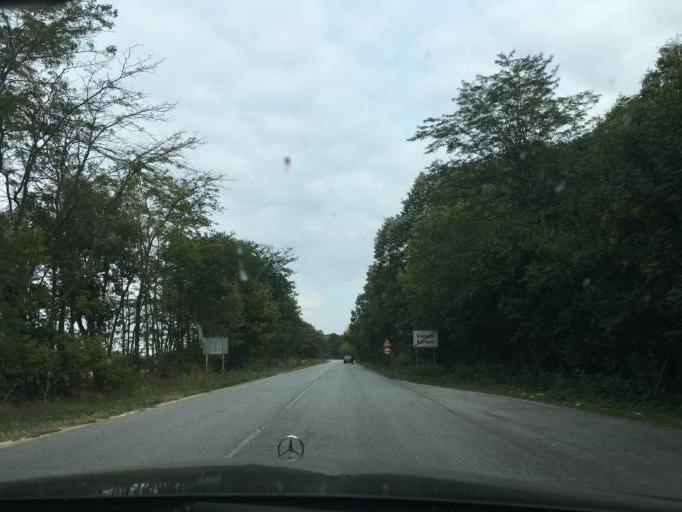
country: RO
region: Constanta
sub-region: Comuna Cerchezu
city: Cerchezu
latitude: 43.7580
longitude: 28.1146
